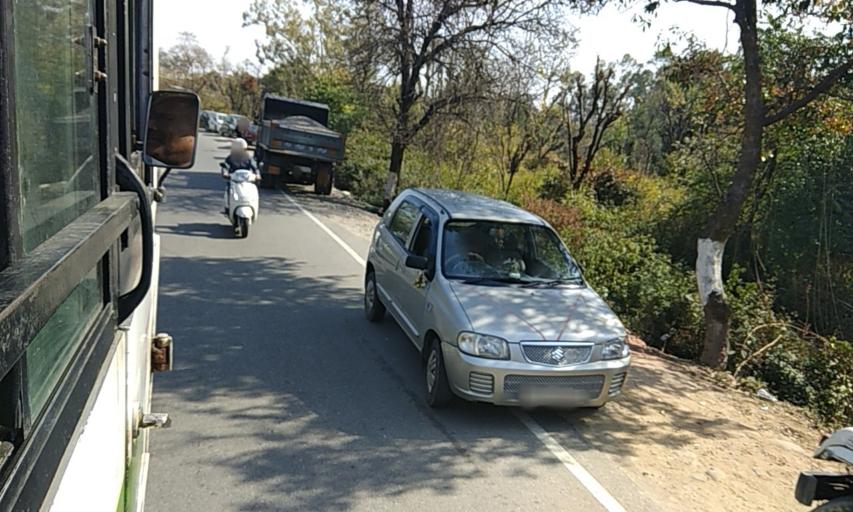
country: IN
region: Himachal Pradesh
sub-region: Kangra
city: Dharmsala
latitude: 32.1869
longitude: 76.3617
